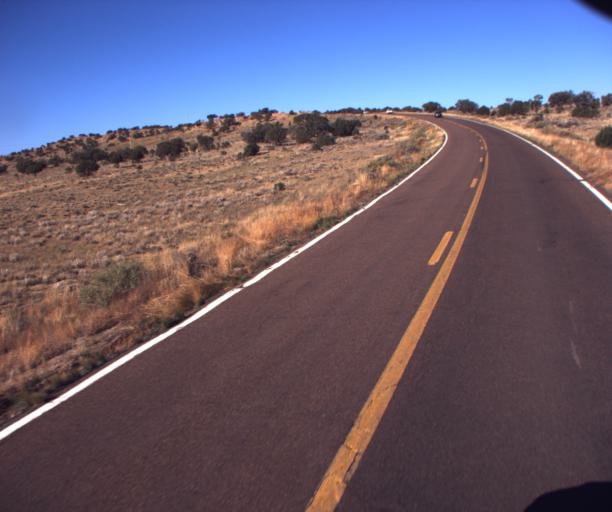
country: US
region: Arizona
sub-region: Apache County
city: Ganado
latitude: 35.7543
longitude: -109.8945
